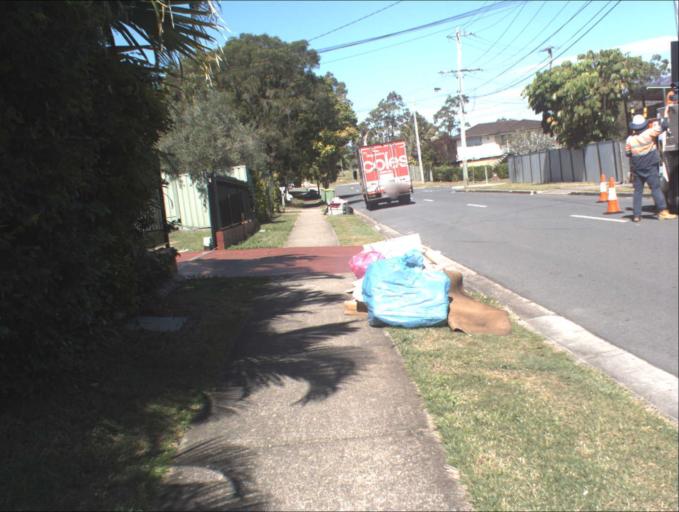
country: AU
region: Queensland
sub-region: Logan
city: Logan City
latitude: -27.6495
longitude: 153.1280
